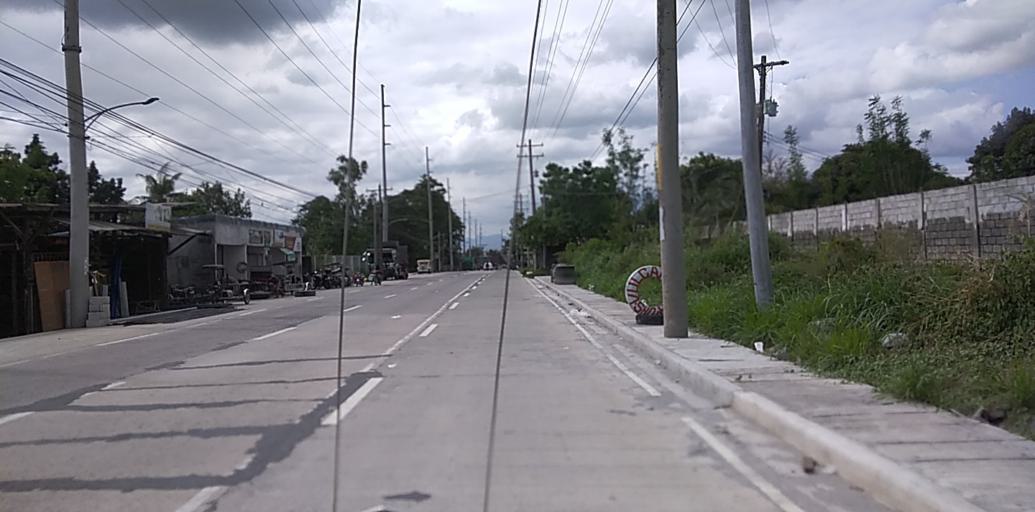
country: PH
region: Central Luzon
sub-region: Province of Pampanga
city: Pio
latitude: 15.0515
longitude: 120.5328
